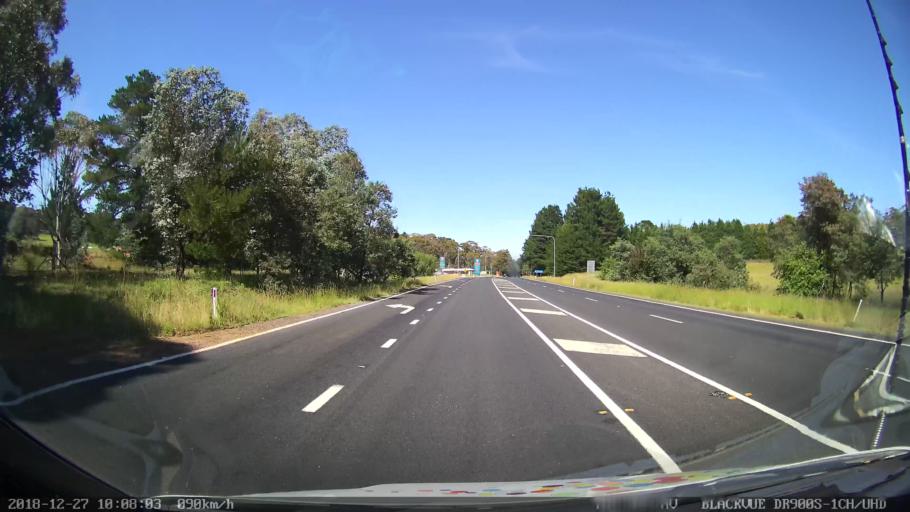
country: AU
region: New South Wales
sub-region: Lithgow
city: Portland
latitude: -33.4452
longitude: 149.8313
